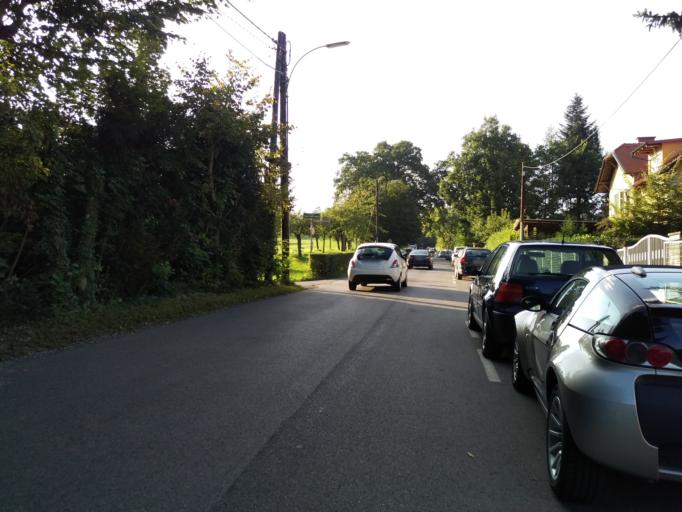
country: AT
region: Styria
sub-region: Graz Stadt
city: Graz
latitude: 47.0865
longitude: 15.4512
